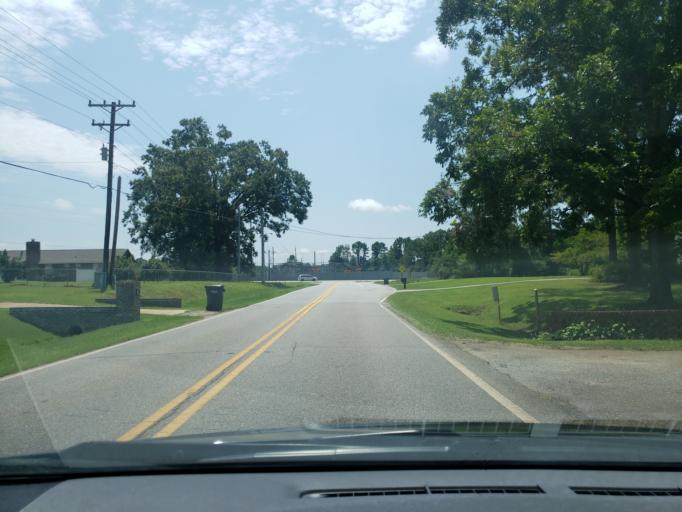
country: US
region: Georgia
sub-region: Dougherty County
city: Albany
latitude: 31.5870
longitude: -84.2811
